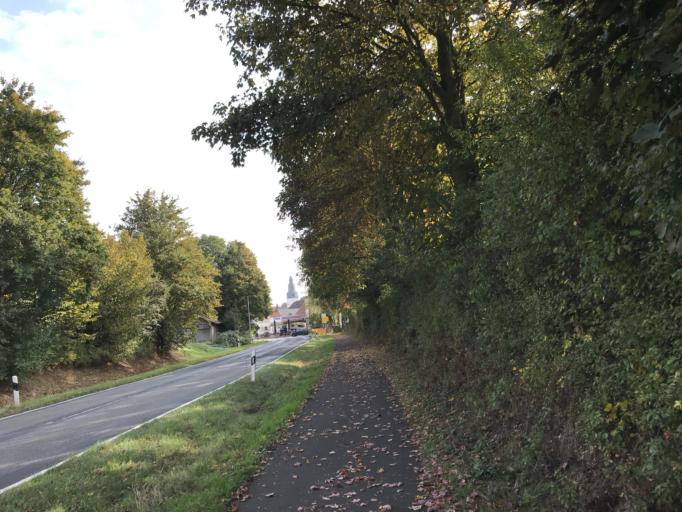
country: DE
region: Hesse
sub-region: Regierungsbezirk Giessen
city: Langgons
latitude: 50.5020
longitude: 8.6569
